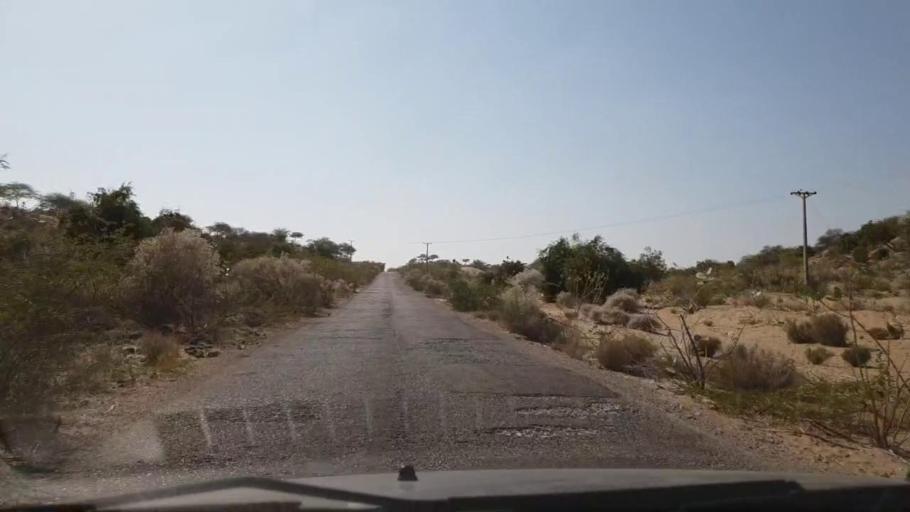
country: PK
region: Sindh
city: Diplo
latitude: 24.5442
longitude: 69.6483
